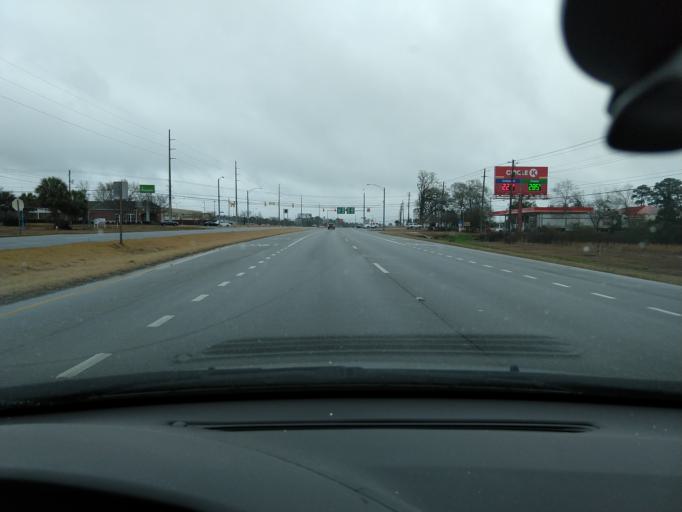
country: US
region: Alabama
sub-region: Houston County
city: Dothan
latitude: 31.2534
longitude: -85.3935
